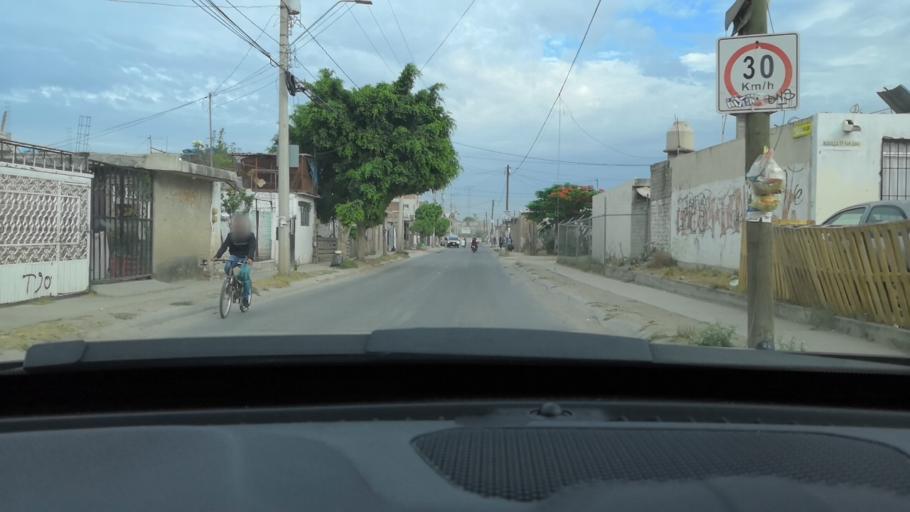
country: MX
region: Guanajuato
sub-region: Leon
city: Fraccionamiento Paraiso Real
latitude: 21.0947
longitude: -101.5920
